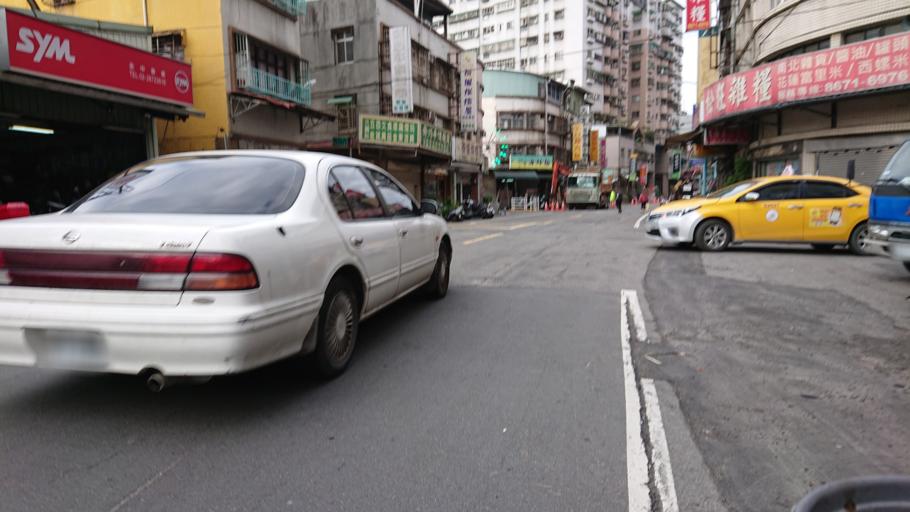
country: TW
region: Taiwan
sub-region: Taoyuan
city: Taoyuan
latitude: 24.9293
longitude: 121.3716
